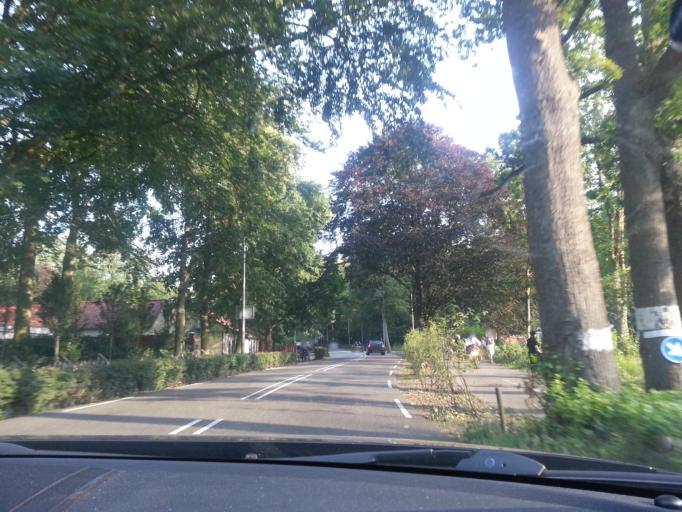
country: NL
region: South Holland
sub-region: Gemeente Lisse
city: Lisse
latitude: 52.2692
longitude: 4.5423
